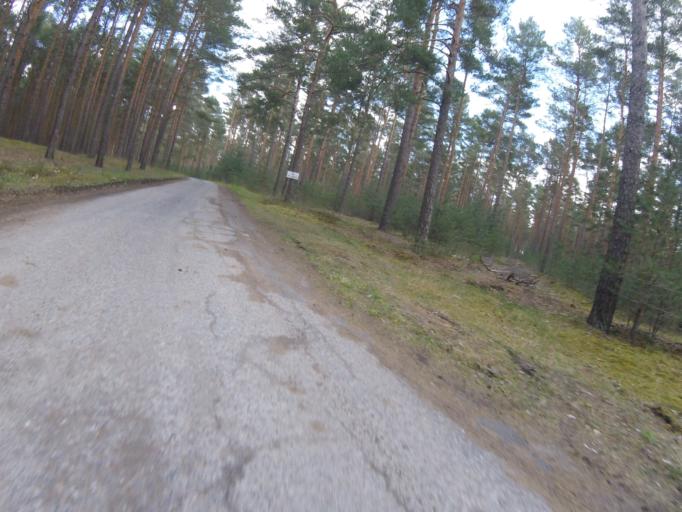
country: DE
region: Brandenburg
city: Gross Koris
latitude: 52.1836
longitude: 13.6842
